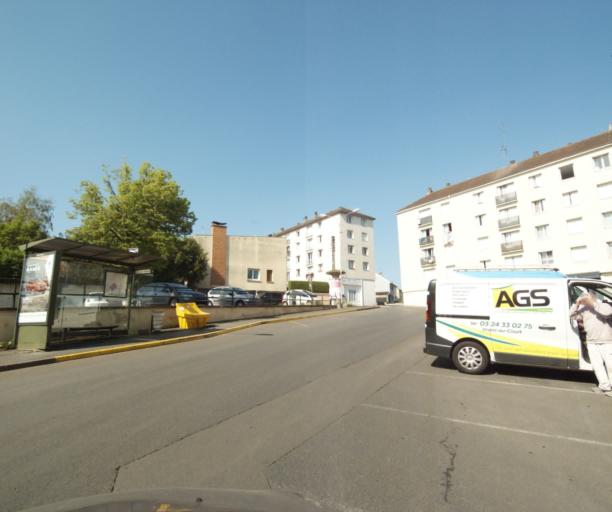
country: FR
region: Champagne-Ardenne
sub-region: Departement des Ardennes
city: Charleville-Mezieres
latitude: 49.7791
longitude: 4.7060
